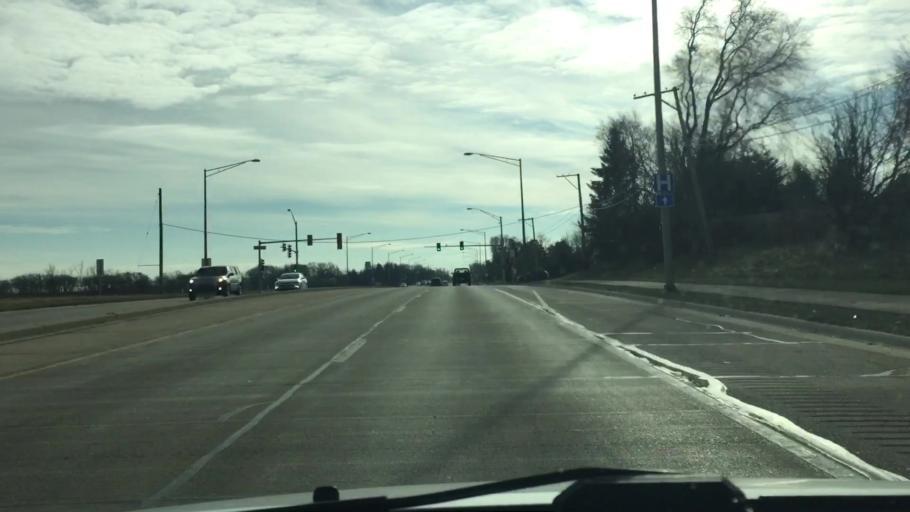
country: US
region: Illinois
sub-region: Kane County
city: Geneva
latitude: 41.9000
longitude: -88.2770
